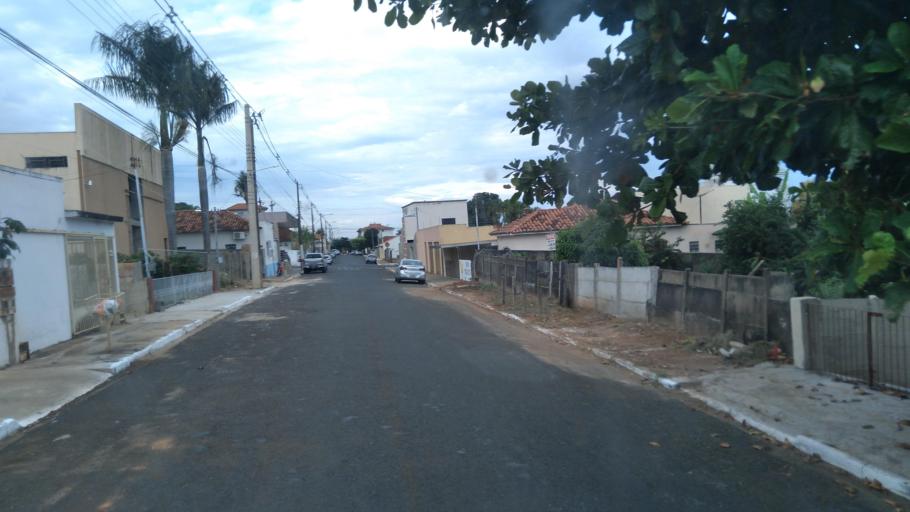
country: BR
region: Goias
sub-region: Mineiros
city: Mineiros
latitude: -17.5682
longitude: -52.5582
